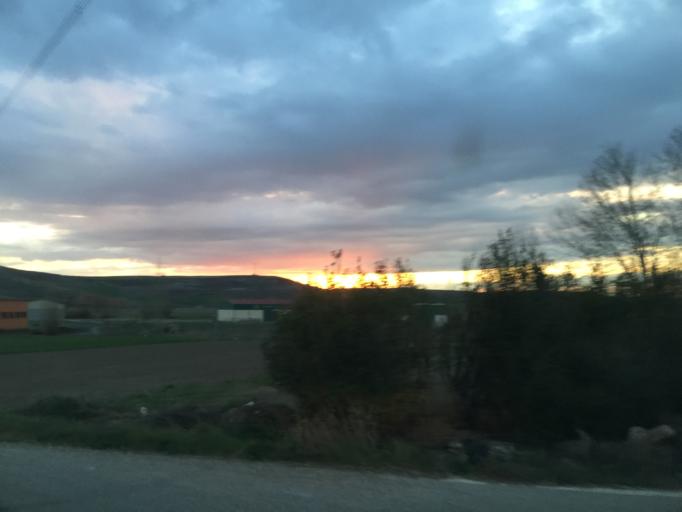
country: ES
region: Castille and Leon
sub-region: Provincia de Burgos
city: Tardajos
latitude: 42.3518
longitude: -3.8190
